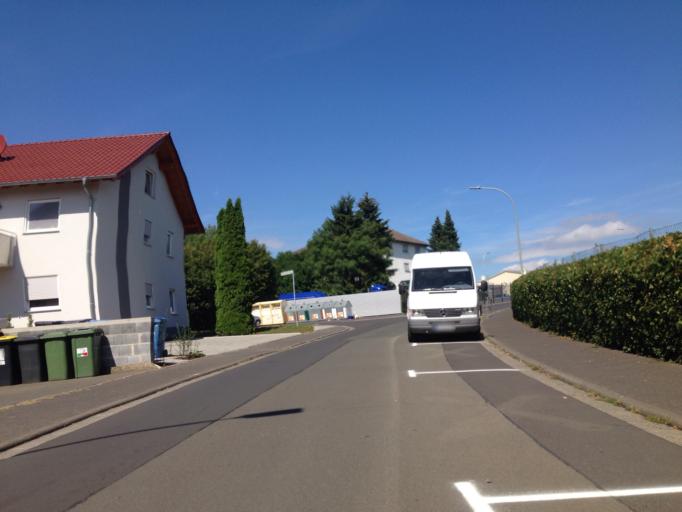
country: DE
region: Hesse
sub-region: Regierungsbezirk Giessen
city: Grunberg
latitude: 50.5934
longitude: 8.9481
